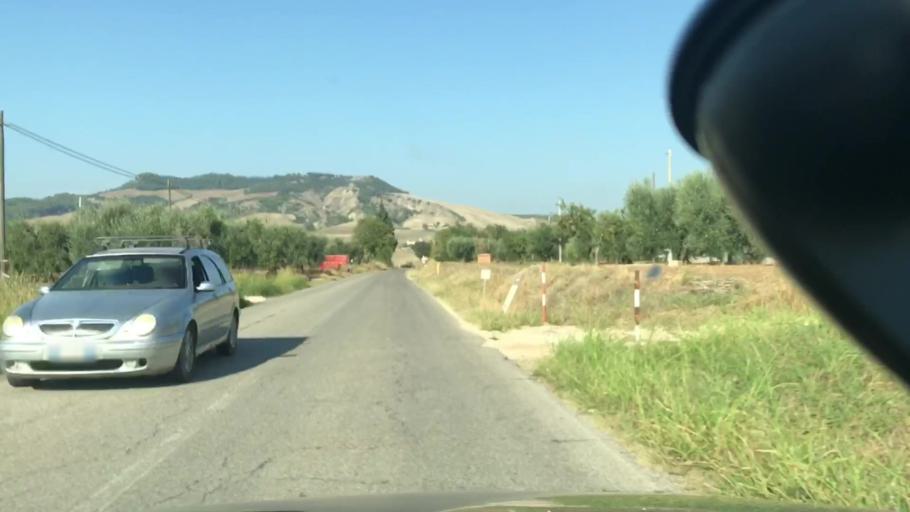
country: IT
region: Basilicate
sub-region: Provincia di Matera
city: La Martella
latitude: 40.6583
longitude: 16.5262
